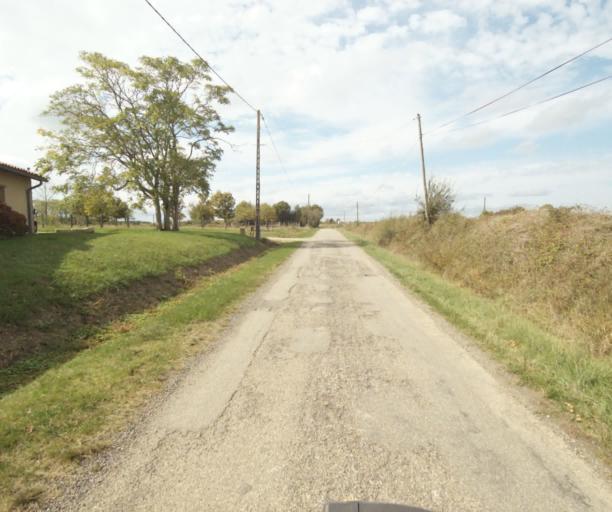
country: FR
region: Midi-Pyrenees
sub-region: Departement du Tarn-et-Garonne
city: Verdun-sur-Garonne
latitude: 43.8620
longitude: 1.1726
